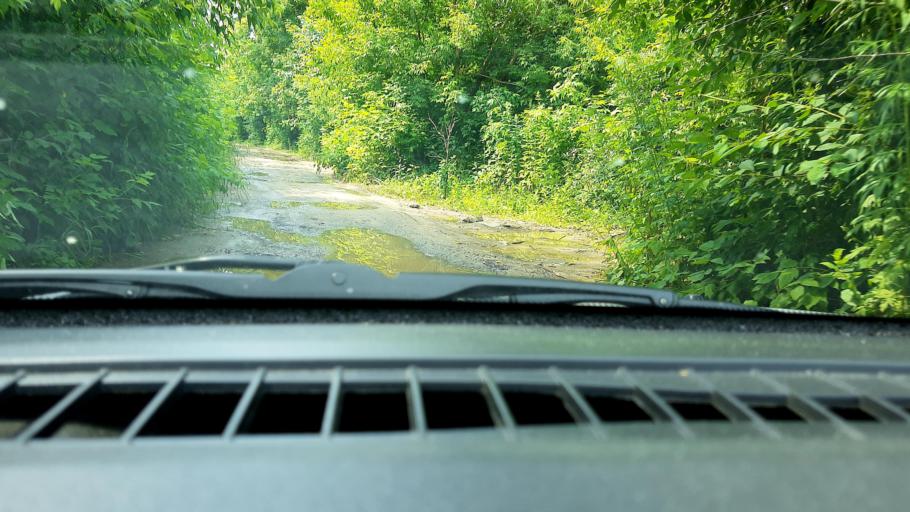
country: RU
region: Nizjnij Novgorod
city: Neklyudovo
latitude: 56.3985
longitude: 43.8486
